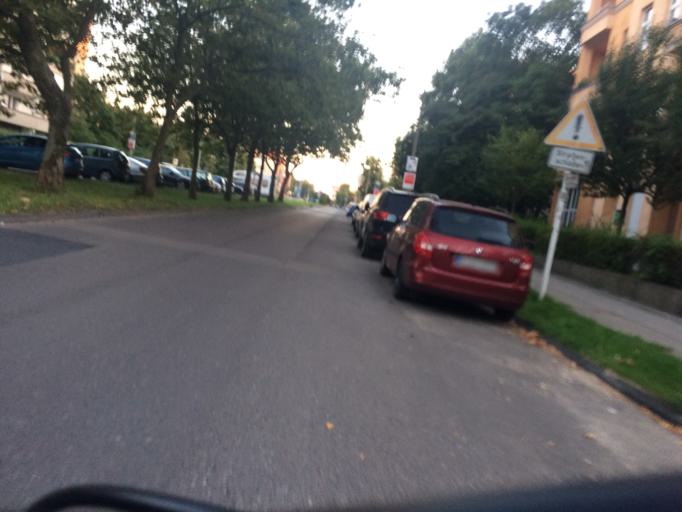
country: DE
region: Berlin
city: Heinersdorf
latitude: 52.5637
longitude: 13.4211
